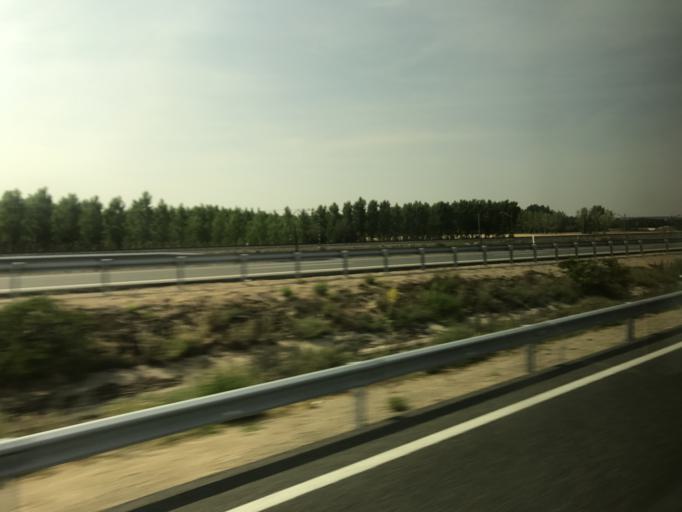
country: ES
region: Castille and Leon
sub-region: Provincia de Burgos
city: Villaverde-Mogina
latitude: 42.1846
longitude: -4.0427
